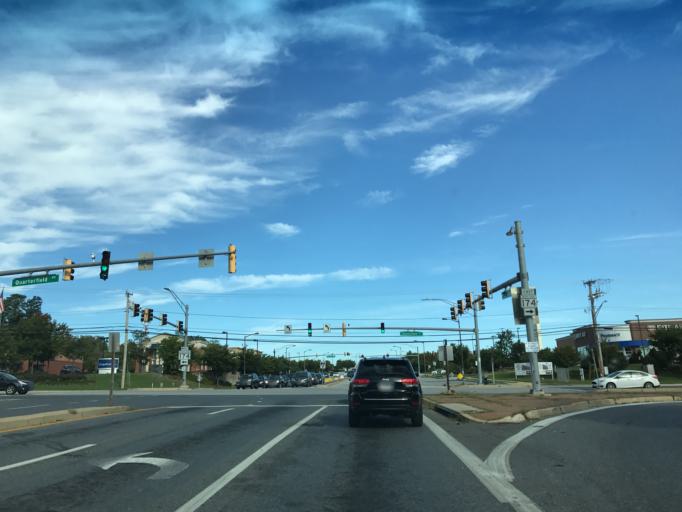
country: US
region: Maryland
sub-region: Anne Arundel County
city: South Gate
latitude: 39.1433
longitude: -76.6469
